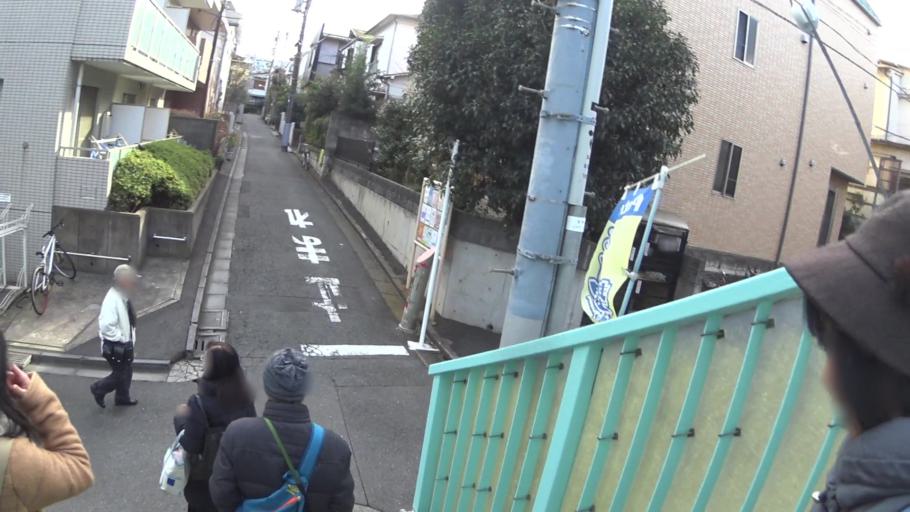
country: JP
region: Tokyo
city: Tokyo
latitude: 35.6702
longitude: 139.6854
